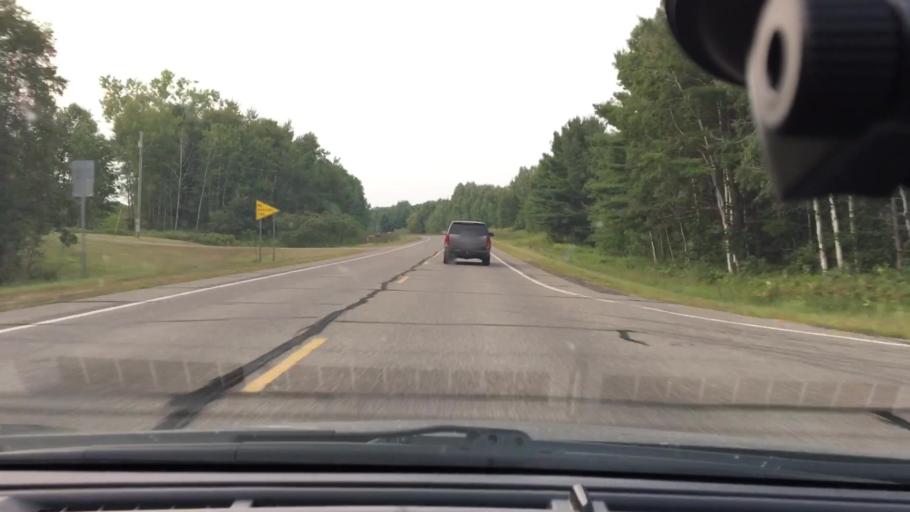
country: US
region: Minnesota
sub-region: Crow Wing County
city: Crosby
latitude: 46.4329
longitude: -93.8736
